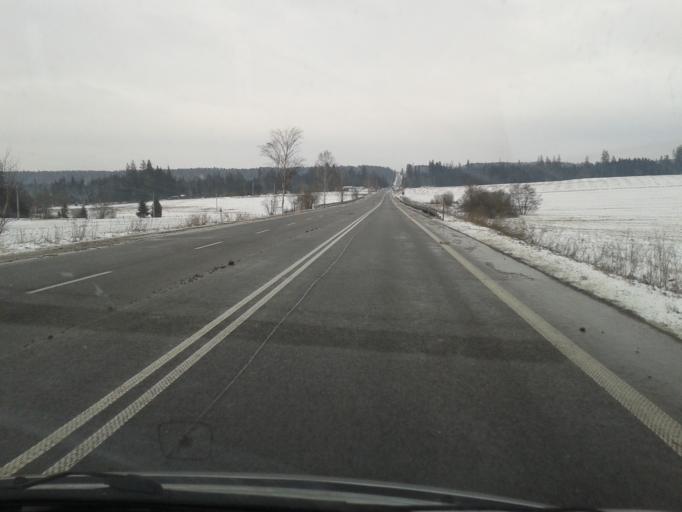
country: PL
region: Lesser Poland Voivodeship
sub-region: Powiat nowotarski
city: Chyzne
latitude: 49.3958
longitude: 19.6466
